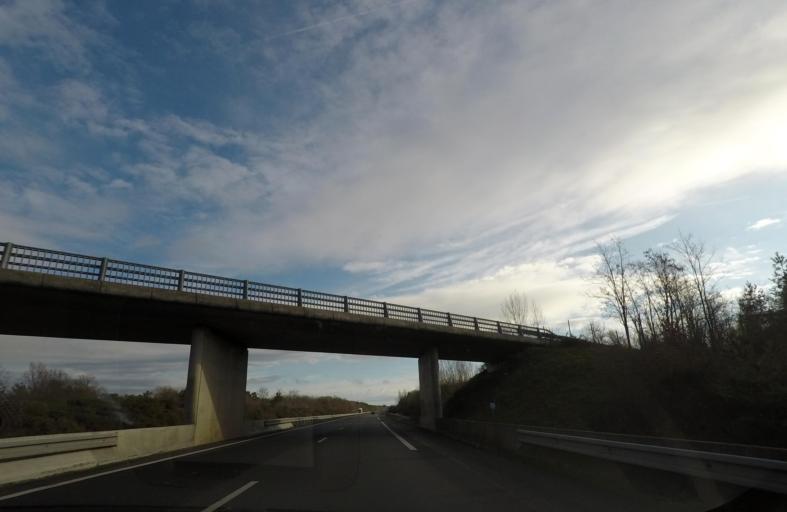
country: FR
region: Centre
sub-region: Departement du Loir-et-Cher
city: Villefranche-sur-Cher
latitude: 47.3184
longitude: 1.7930
